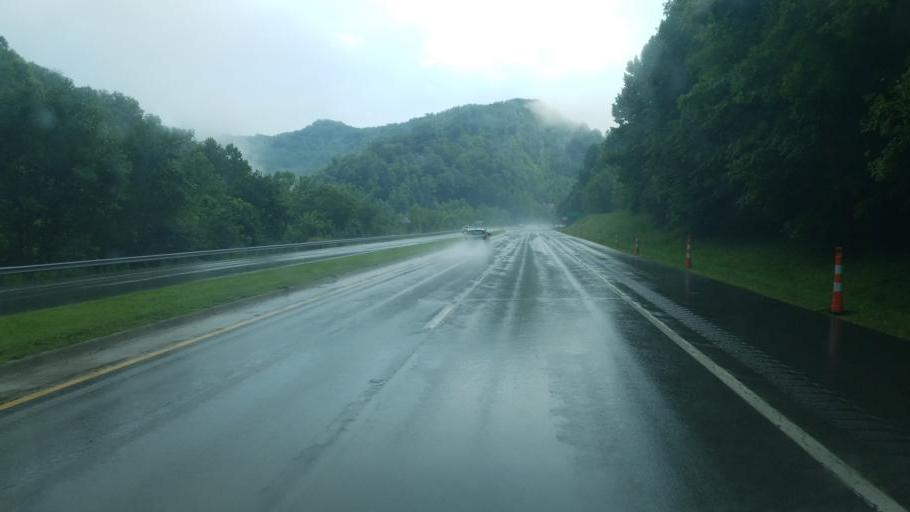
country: US
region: West Virginia
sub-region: Logan County
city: Chapmanville
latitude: 37.9766
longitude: -81.9961
